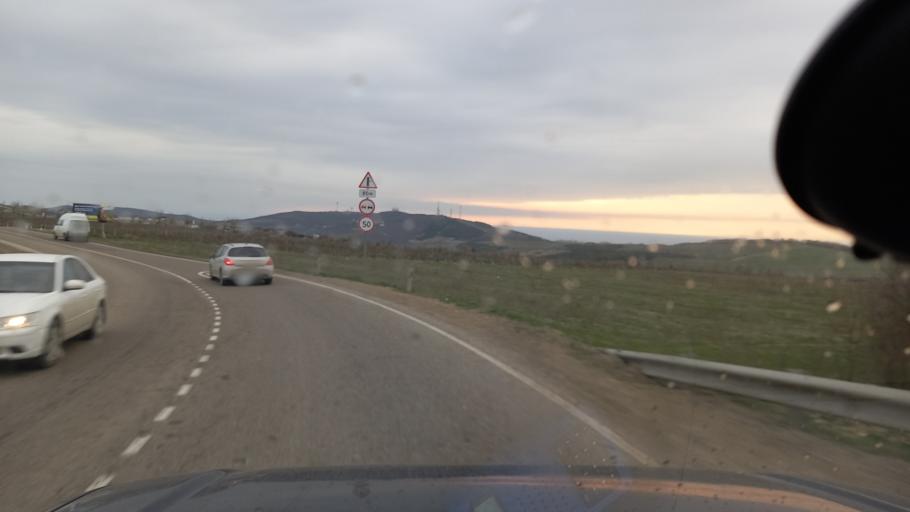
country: RU
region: Krasnodarskiy
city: Sukko
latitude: 44.8414
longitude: 37.4004
